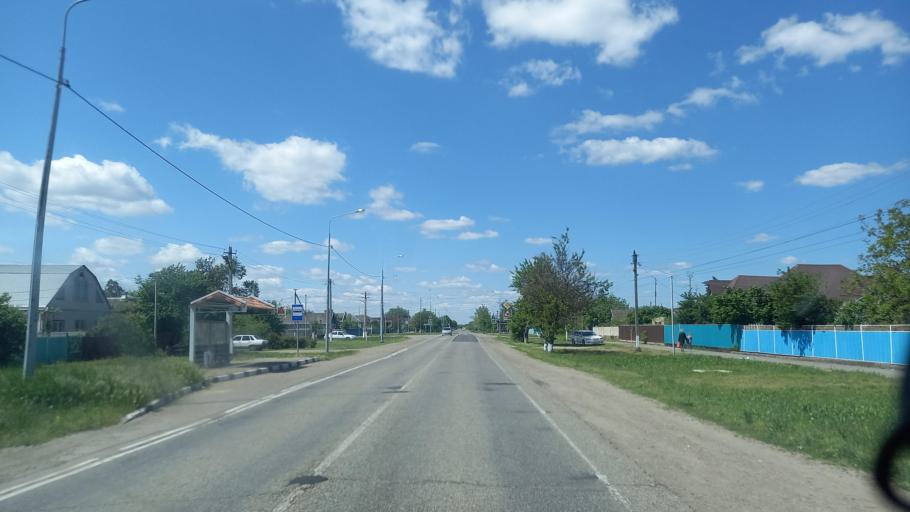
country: RU
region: Krasnodarskiy
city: Tbilisskaya
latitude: 45.3288
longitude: 40.2834
